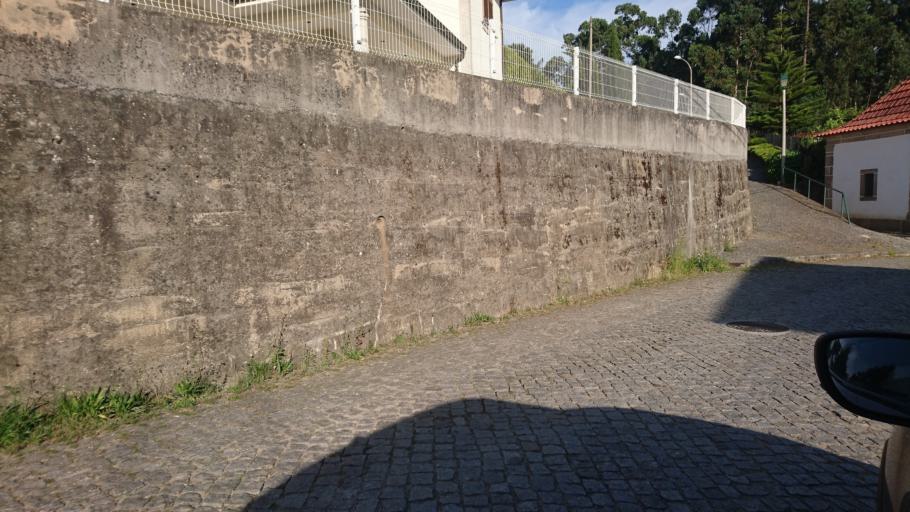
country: PT
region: Porto
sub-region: Paredes
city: Recarei
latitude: 41.1266
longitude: -8.3683
